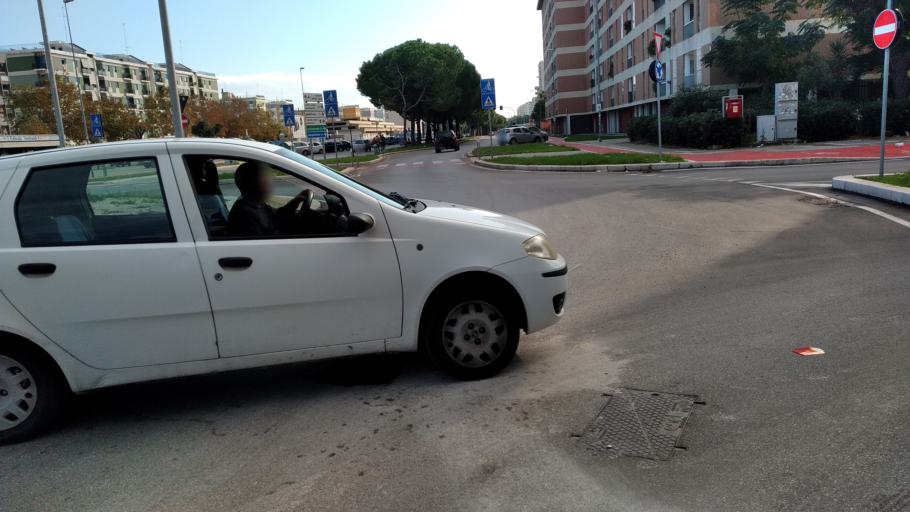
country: IT
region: Apulia
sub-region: Provincia di Bari
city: Bari
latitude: 41.1086
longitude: 16.8935
